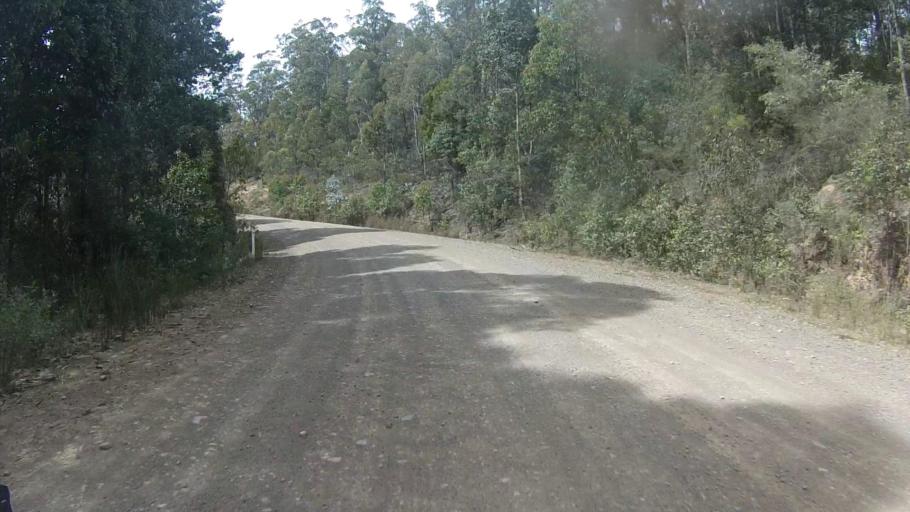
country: AU
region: Tasmania
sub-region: Sorell
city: Sorell
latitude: -42.7607
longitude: 147.8290
